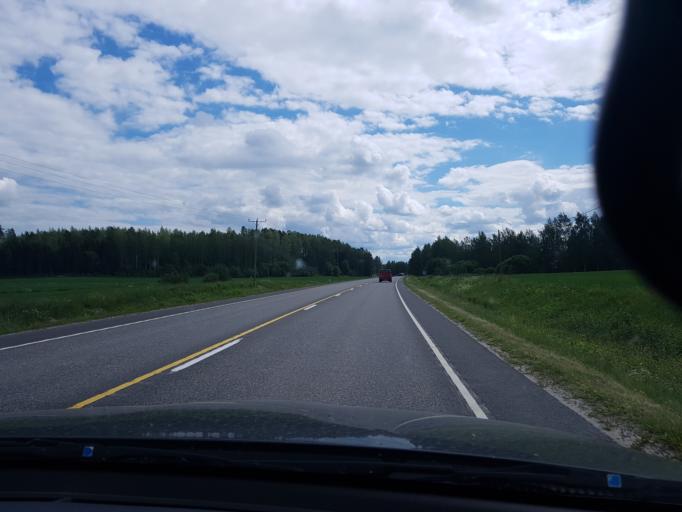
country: FI
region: Pirkanmaa
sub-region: Tampere
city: Paelkaene
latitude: 61.2824
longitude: 24.3353
